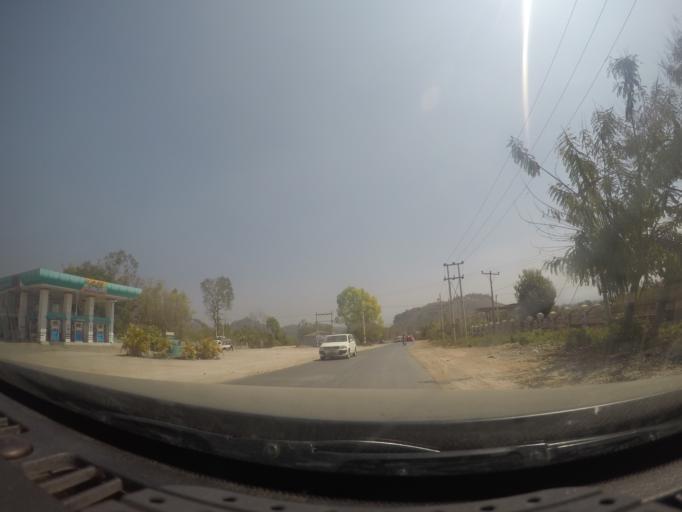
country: MM
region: Shan
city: Taunggyi
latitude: 20.7754
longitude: 97.1306
